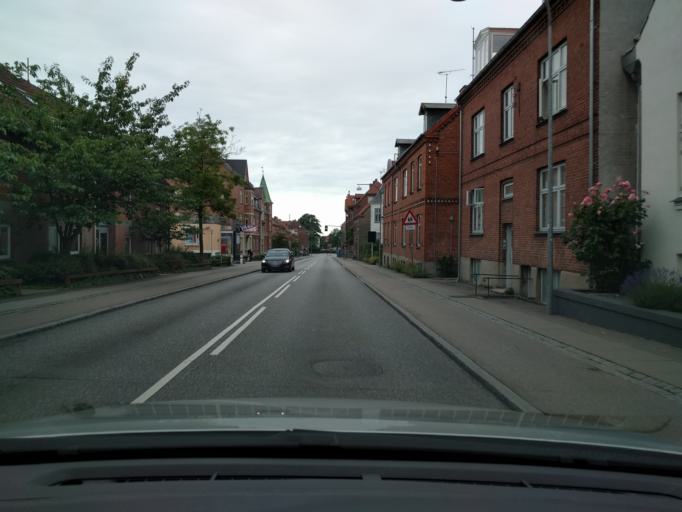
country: DK
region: Zealand
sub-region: Roskilde Kommune
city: Roskilde
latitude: 55.6385
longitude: 12.0748
